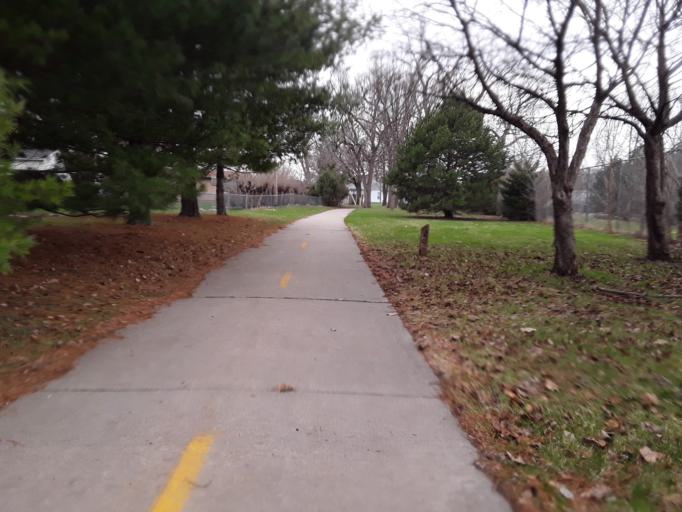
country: US
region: Nebraska
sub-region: Lancaster County
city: Lincoln
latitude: 40.8449
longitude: -96.6623
